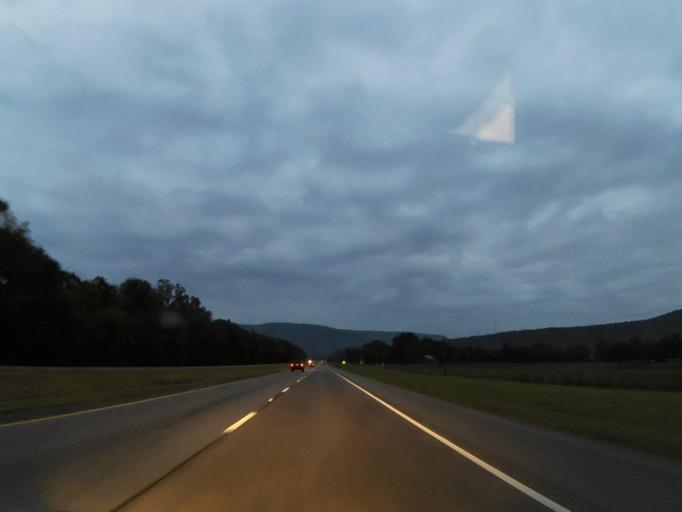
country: US
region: Alabama
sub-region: Madison County
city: Owens Cross Roads
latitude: 34.6874
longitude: -86.3455
